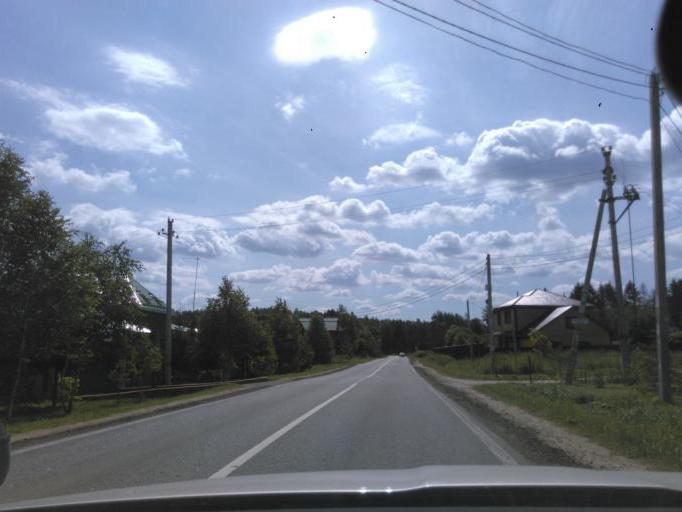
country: RU
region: Moskovskaya
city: Solnechnogorsk
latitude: 56.1588
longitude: 36.9794
